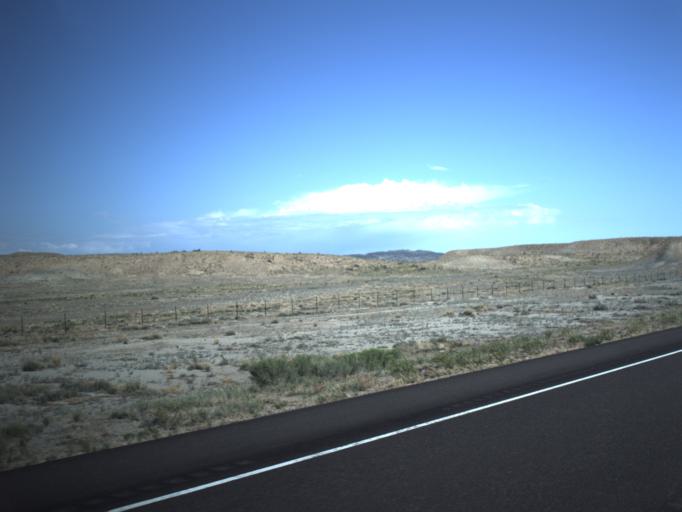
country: US
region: Utah
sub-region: Carbon County
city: East Carbon City
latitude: 39.0820
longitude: -110.3182
